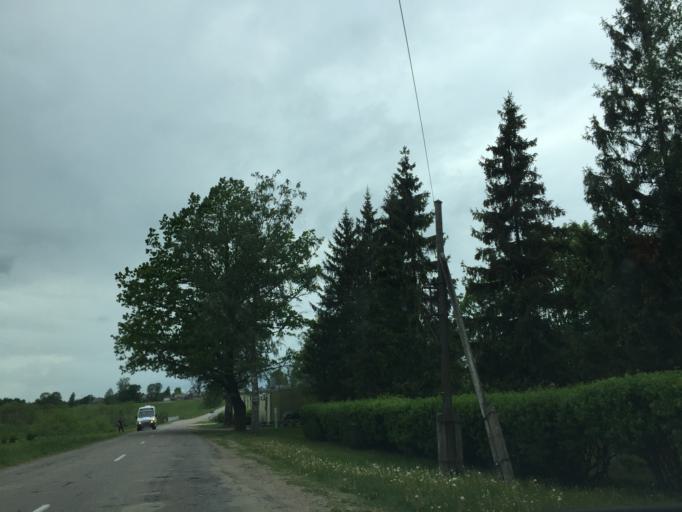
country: LV
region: Varkava
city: Vecvarkava
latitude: 56.0990
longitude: 26.5314
